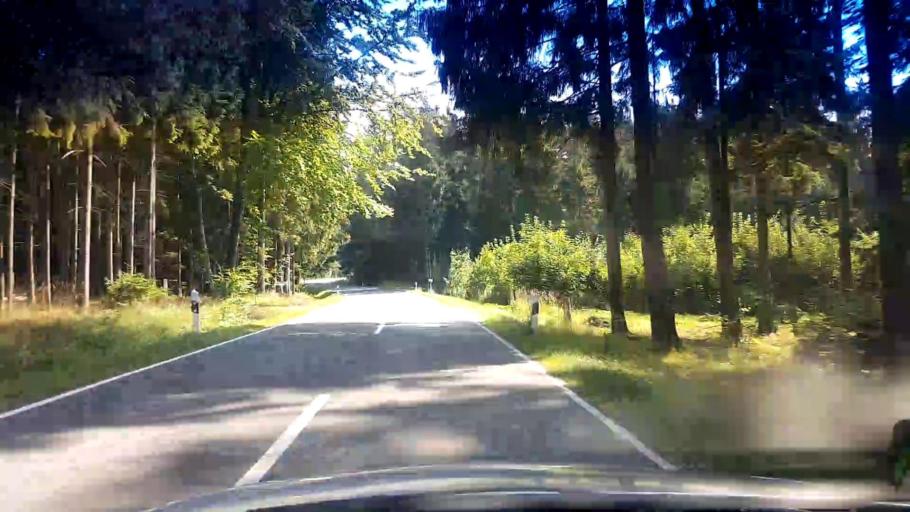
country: DE
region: Bavaria
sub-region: Upper Franconia
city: Stadelhofen
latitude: 49.9752
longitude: 11.2118
